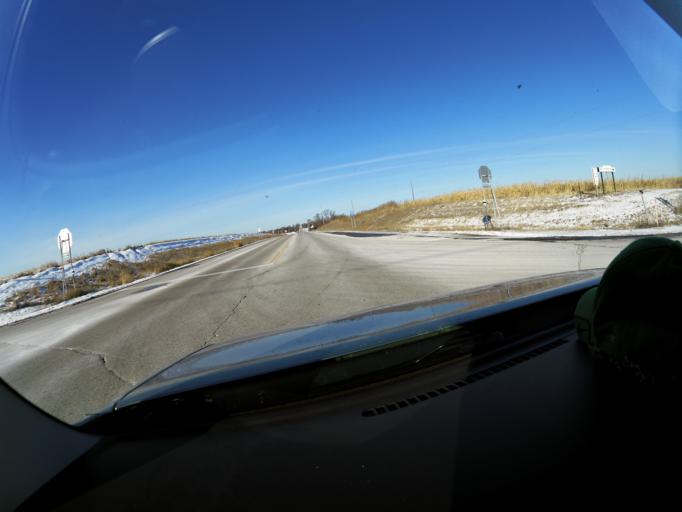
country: US
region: Minnesota
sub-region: Washington County
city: Cottage Grove
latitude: 44.8479
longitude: -92.8626
